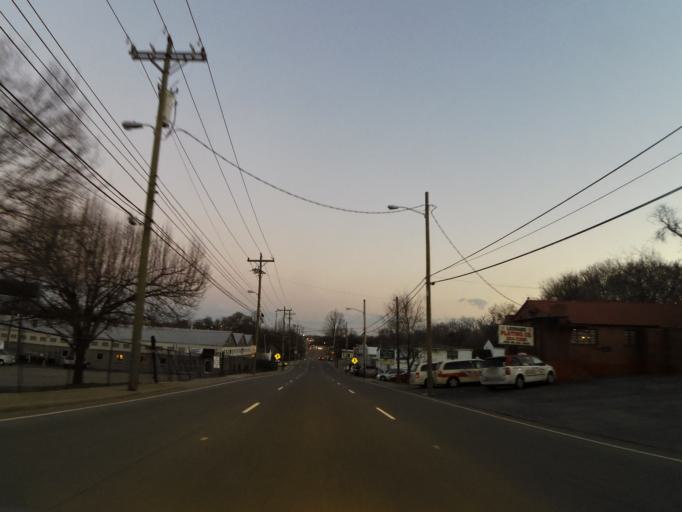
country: US
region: Tennessee
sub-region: Davidson County
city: Nashville
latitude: 36.1399
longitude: -86.7633
